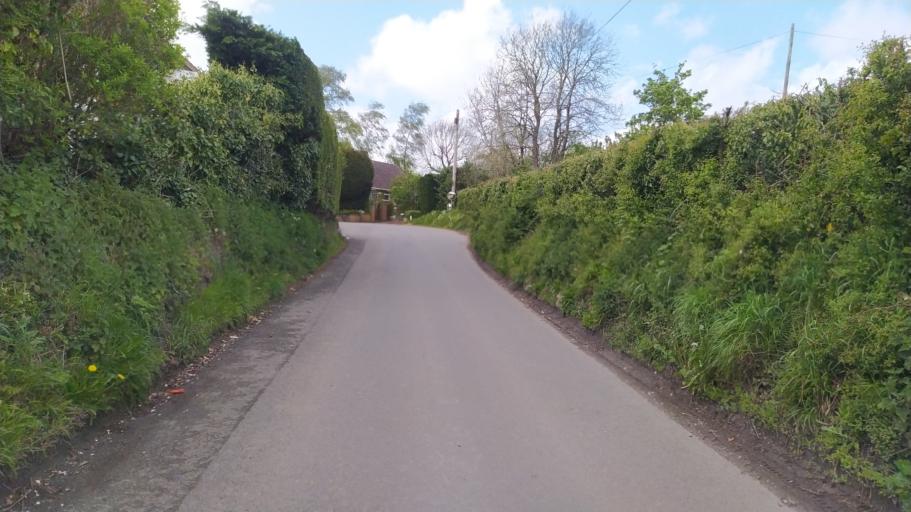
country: GB
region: England
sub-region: Dorset
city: Sturminster Newton
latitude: 50.8980
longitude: -2.2739
